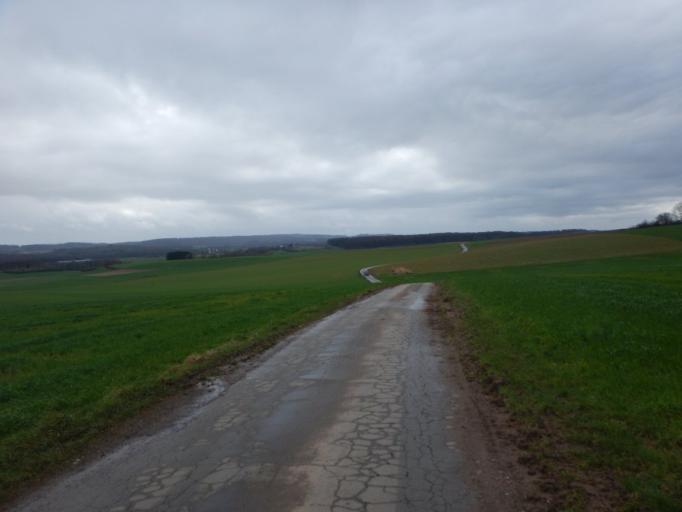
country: BE
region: Wallonia
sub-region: Province du Luxembourg
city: Attert
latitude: 49.7764
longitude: 5.8035
